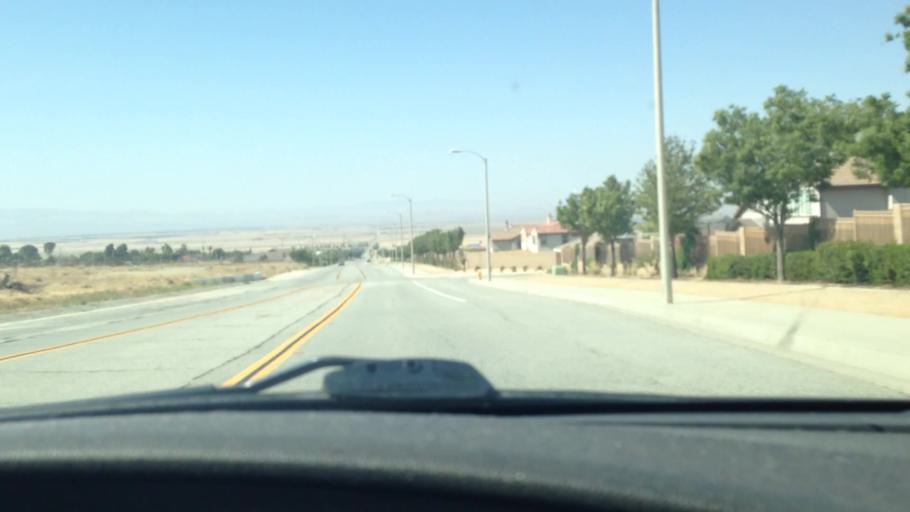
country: US
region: California
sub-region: Los Angeles County
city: Quartz Hill
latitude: 34.6395
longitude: -118.2535
